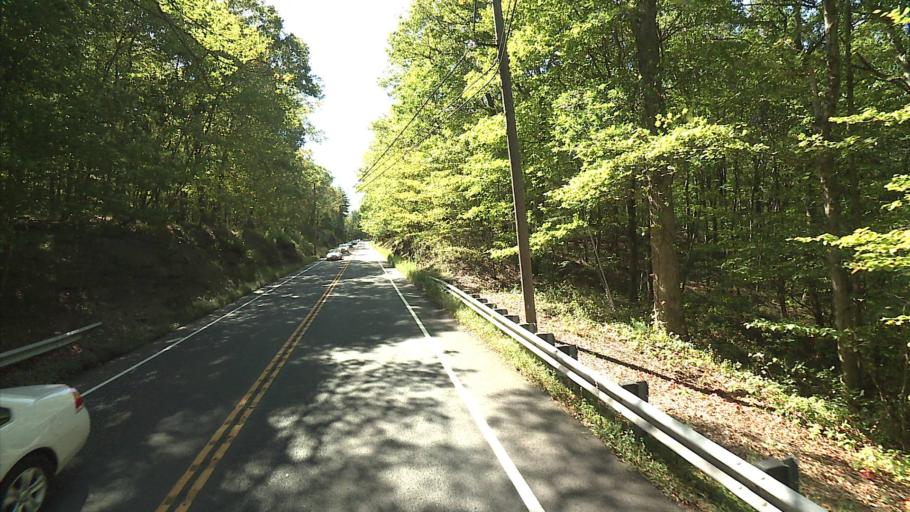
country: US
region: Connecticut
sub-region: New Haven County
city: Prospect
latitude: 41.4537
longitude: -72.9684
